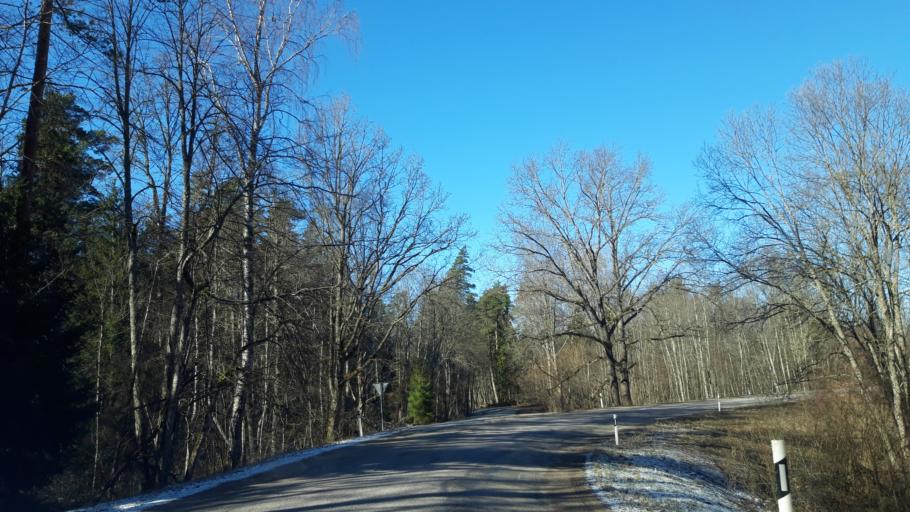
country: LV
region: Strenci
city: Strenci
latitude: 57.6169
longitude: 25.7021
